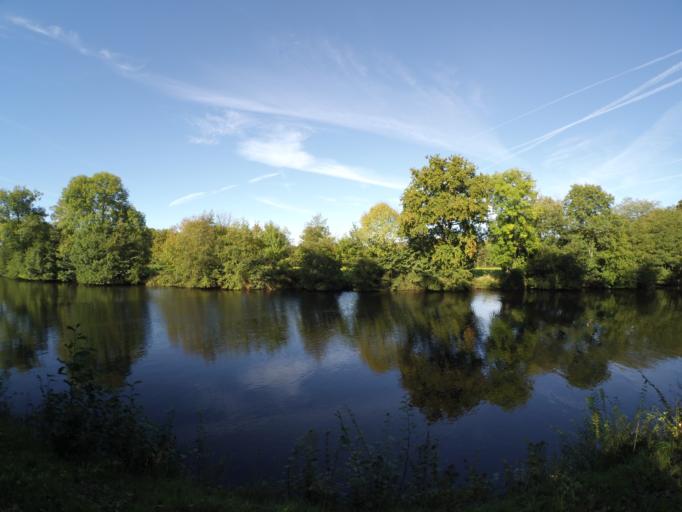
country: FR
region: Brittany
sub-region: Departement du Morbihan
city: Peillac
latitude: 47.7294
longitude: -2.2157
